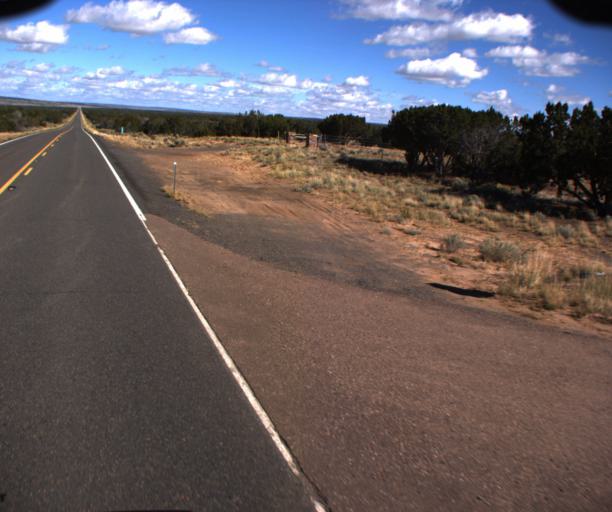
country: US
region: Arizona
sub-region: Apache County
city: Saint Johns
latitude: 34.8495
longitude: -109.2376
